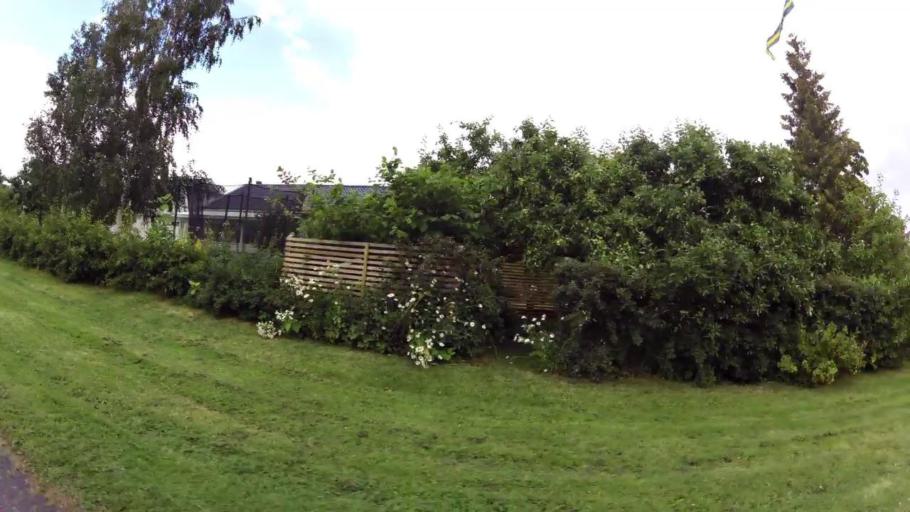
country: SE
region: OEstergoetland
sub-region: Linkopings Kommun
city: Sturefors
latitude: 58.3843
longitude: 15.7054
